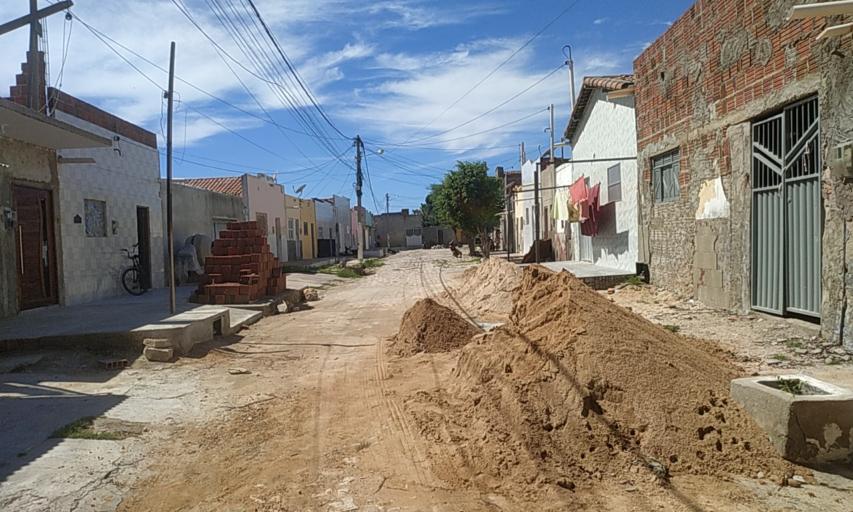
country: BR
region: Rio Grande do Norte
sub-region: Areia Branca
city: Areia Branca
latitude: -4.9591
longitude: -37.1325
